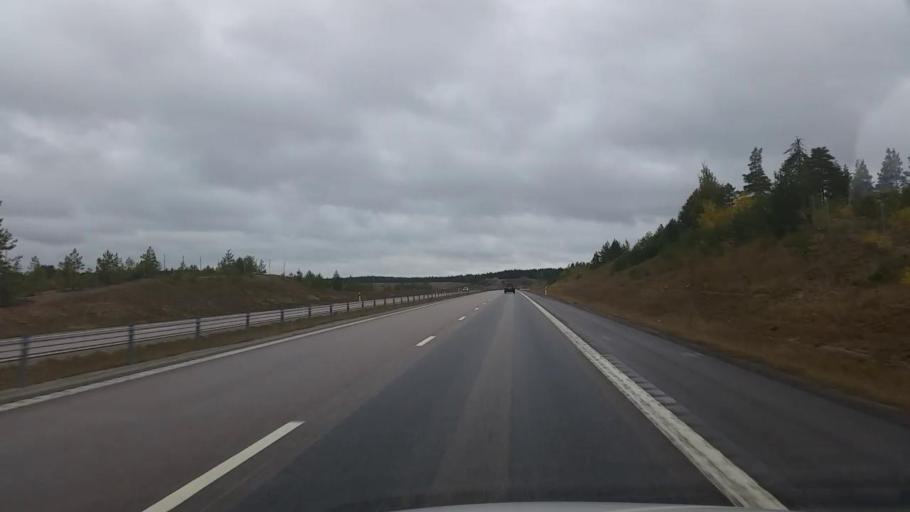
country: SE
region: Uppsala
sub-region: Osthammars Kommun
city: Bjorklinge
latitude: 60.1115
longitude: 17.5549
